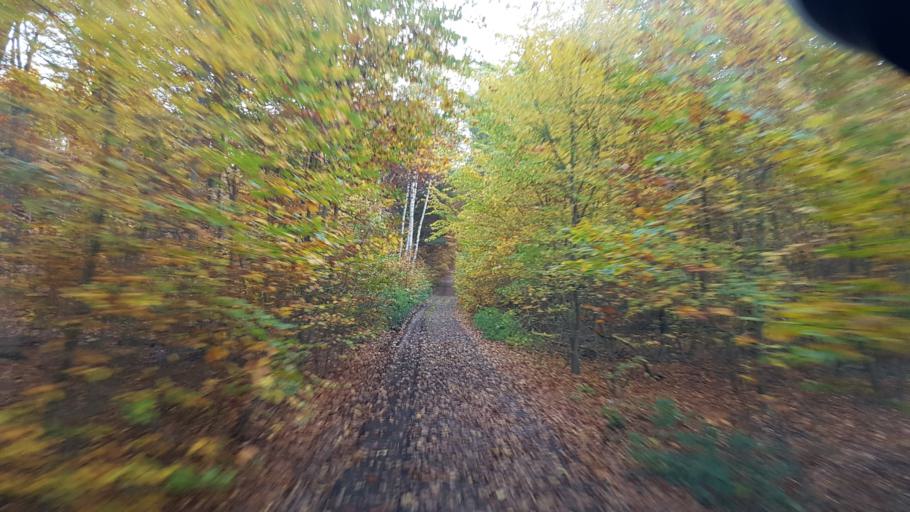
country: DE
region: Saxony
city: Schildau
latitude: 51.4241
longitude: 12.9767
